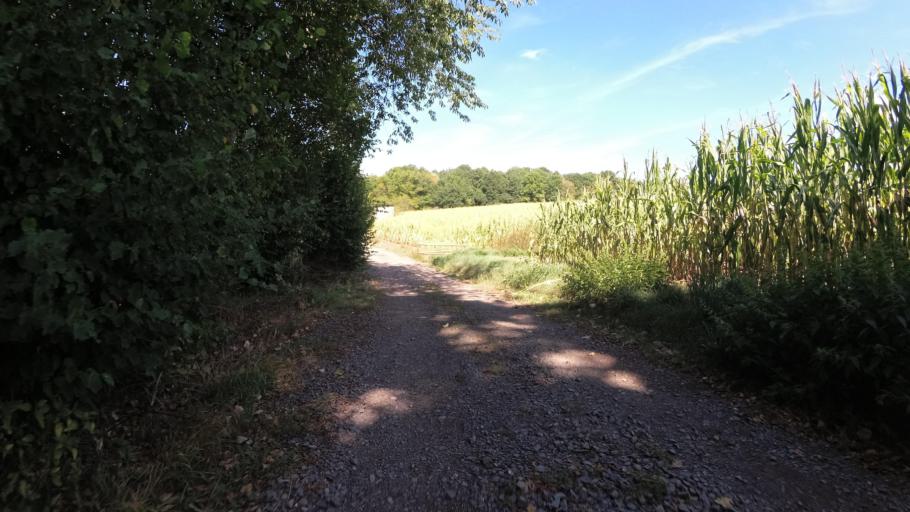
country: DE
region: Saarland
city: Mainzweiler
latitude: 49.4113
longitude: 7.0861
